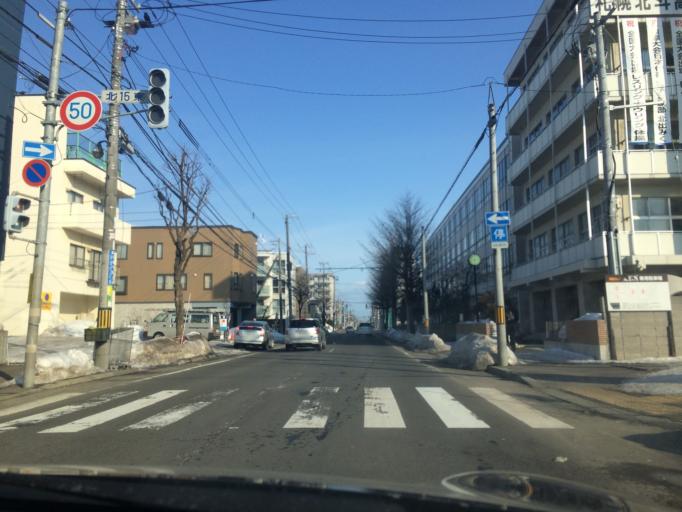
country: JP
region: Hokkaido
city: Sapporo
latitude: 43.0792
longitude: 141.3544
